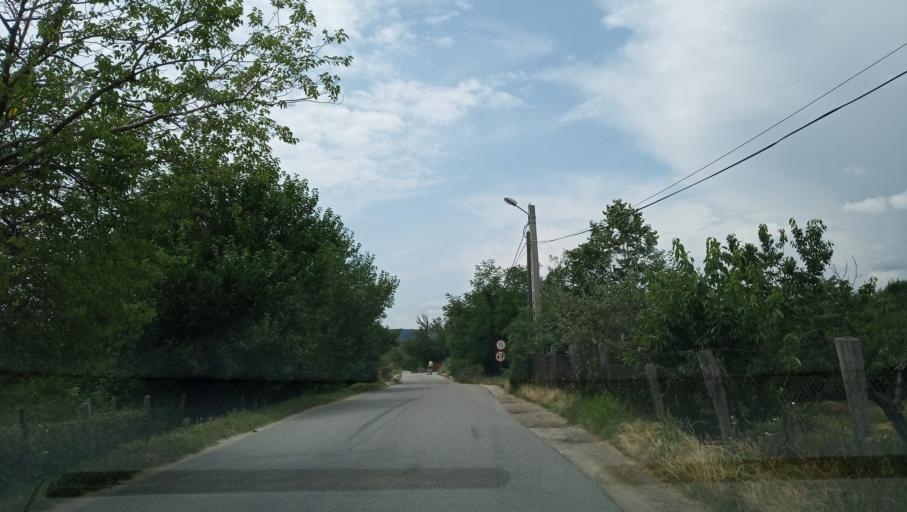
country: RO
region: Gorj
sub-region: Comuna Bumbesti-Jiu
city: Bumbesti-Jiu
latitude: 45.1786
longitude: 23.3679
